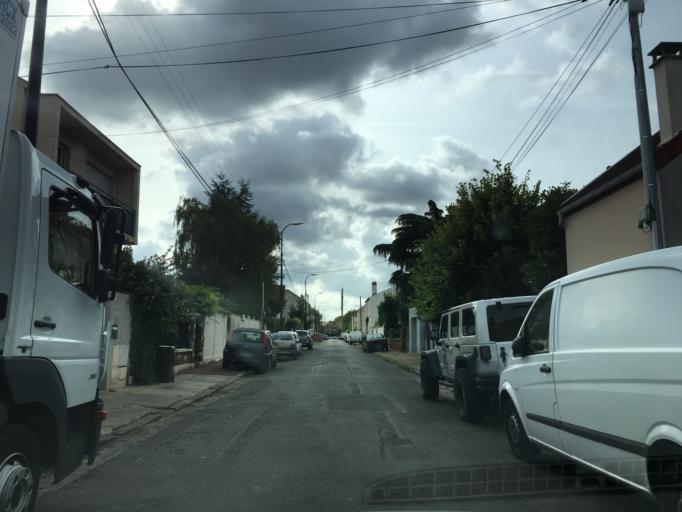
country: FR
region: Ile-de-France
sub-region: Departement du Val-de-Marne
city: Saint-Maur-des-Fosses
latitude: 48.7897
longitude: 2.4905
